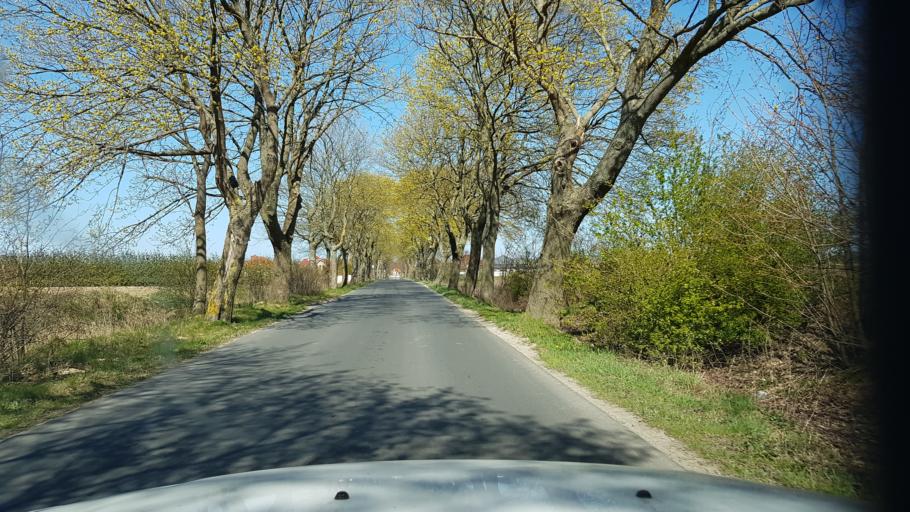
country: PL
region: West Pomeranian Voivodeship
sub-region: Koszalin
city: Koszalin
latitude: 54.2369
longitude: 16.1635
